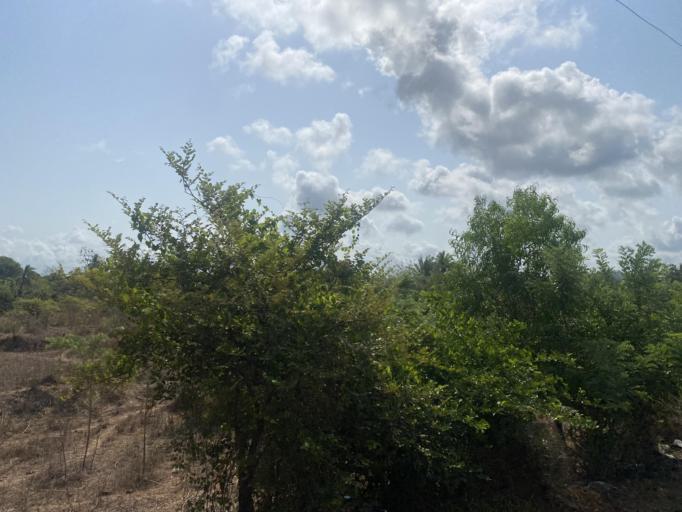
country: IN
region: Daman and Diu
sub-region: Daman District
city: Daman
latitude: 20.3338
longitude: 72.8070
